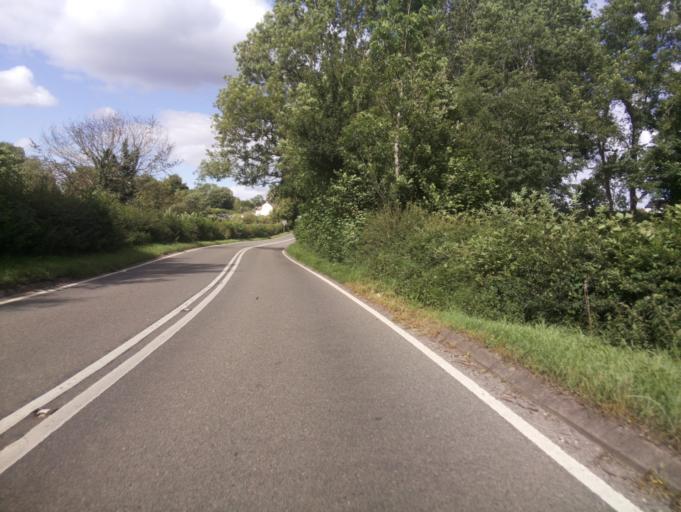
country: GB
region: England
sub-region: Leicestershire
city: Coalville
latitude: 52.7662
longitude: -1.3929
